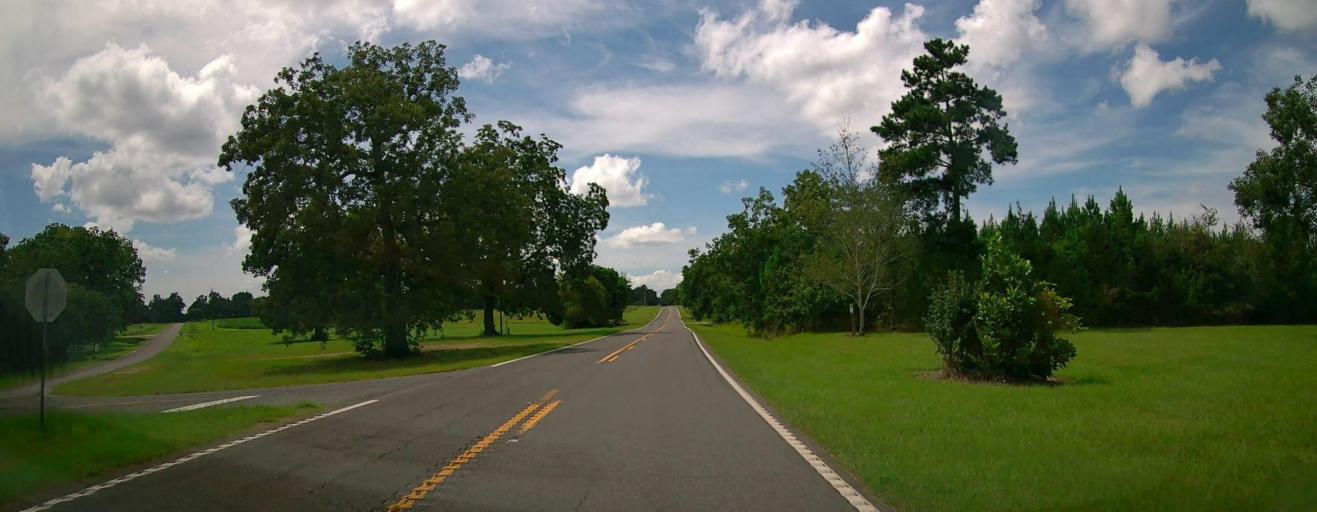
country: US
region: Georgia
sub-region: Taylor County
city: Reynolds
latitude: 32.4400
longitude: -84.1161
